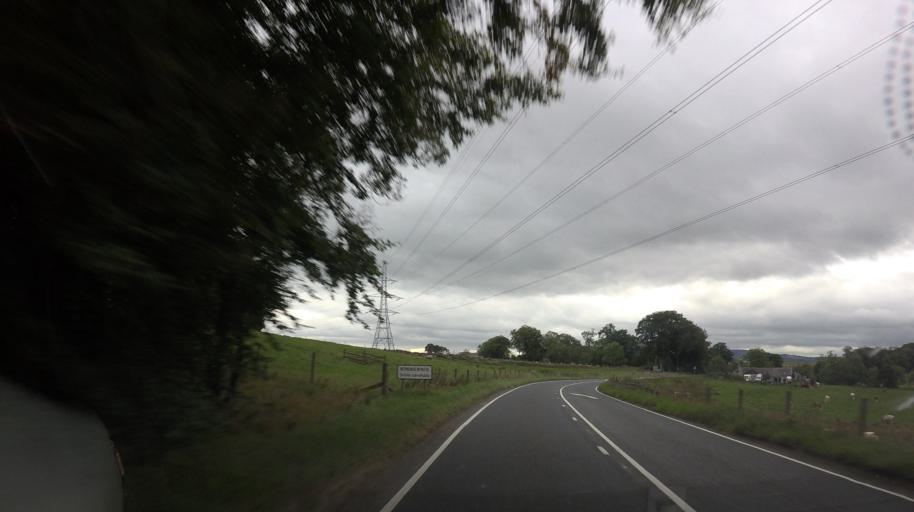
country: GB
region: Scotland
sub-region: Aberdeenshire
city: Kemnay
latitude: 57.1773
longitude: -2.4488
